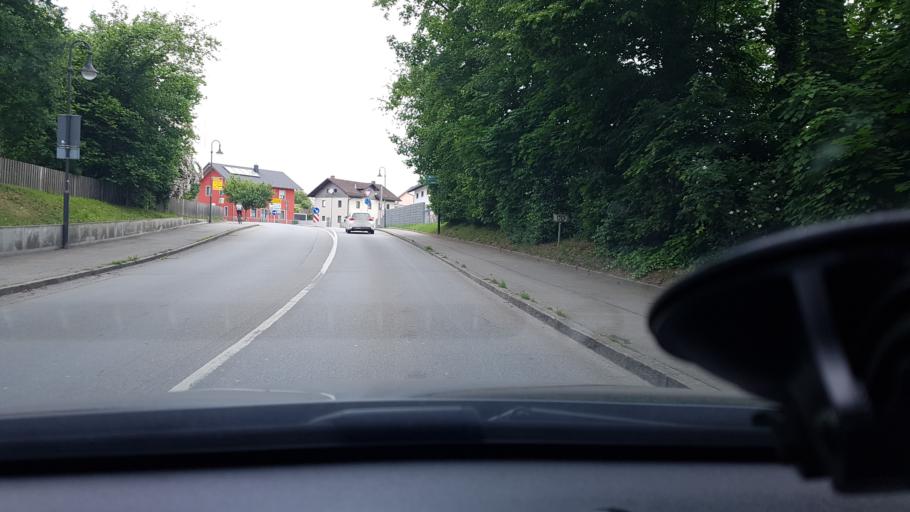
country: DE
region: Bavaria
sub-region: Lower Bavaria
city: Pocking
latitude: 48.3969
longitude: 13.3115
